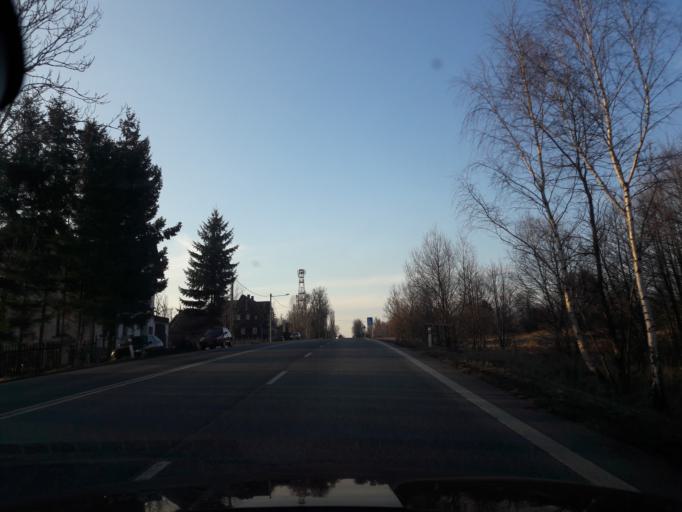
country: CZ
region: Ustecky
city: Dolni Podluzi
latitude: 50.8966
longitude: 14.5716
